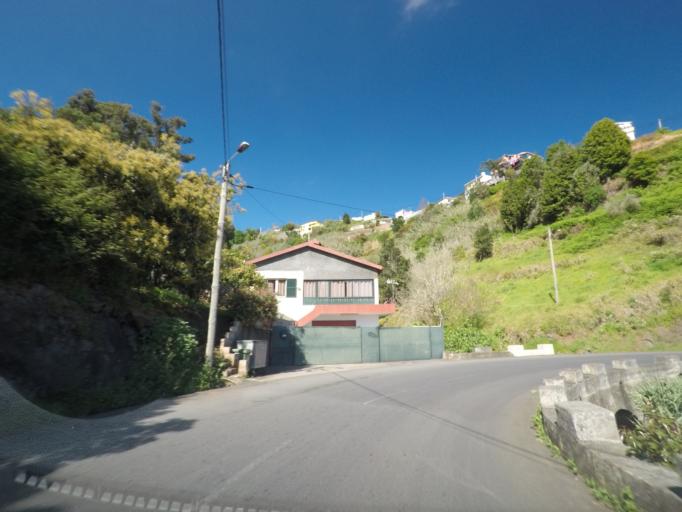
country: PT
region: Madeira
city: Ponta do Sol
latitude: 32.6979
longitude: -17.1026
